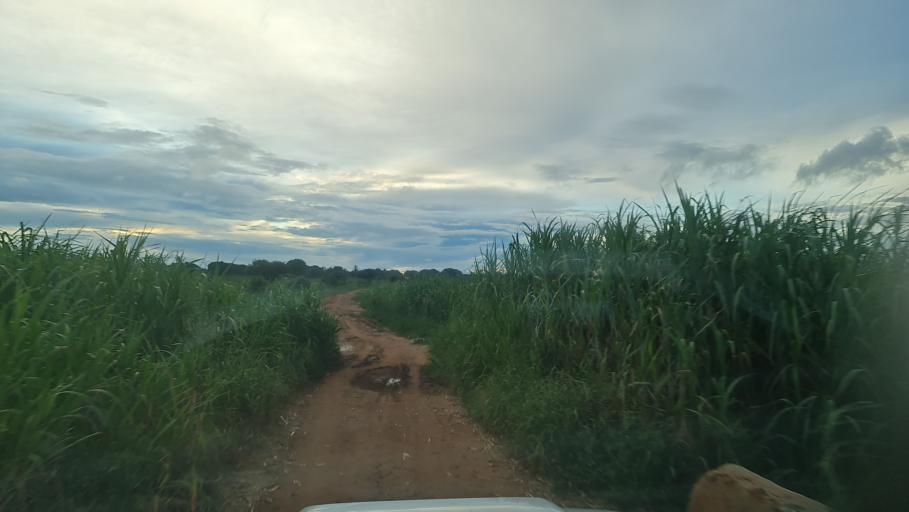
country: MZ
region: Nampula
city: Nacala
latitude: -14.7419
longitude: 39.9481
